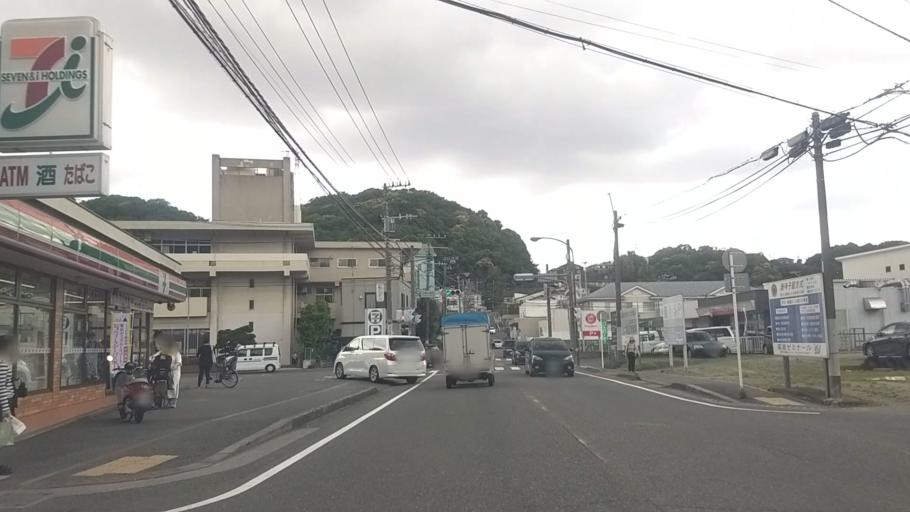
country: JP
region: Kanagawa
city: Kamakura
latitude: 35.3537
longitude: 139.5254
